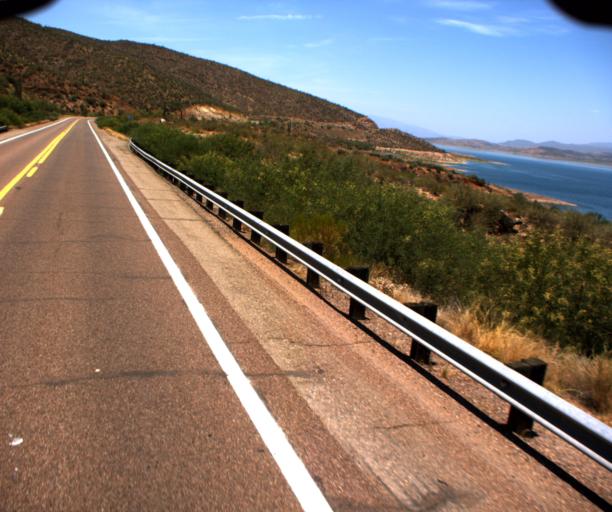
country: US
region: Arizona
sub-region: Gila County
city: Tonto Basin
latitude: 33.6826
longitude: -111.1684
